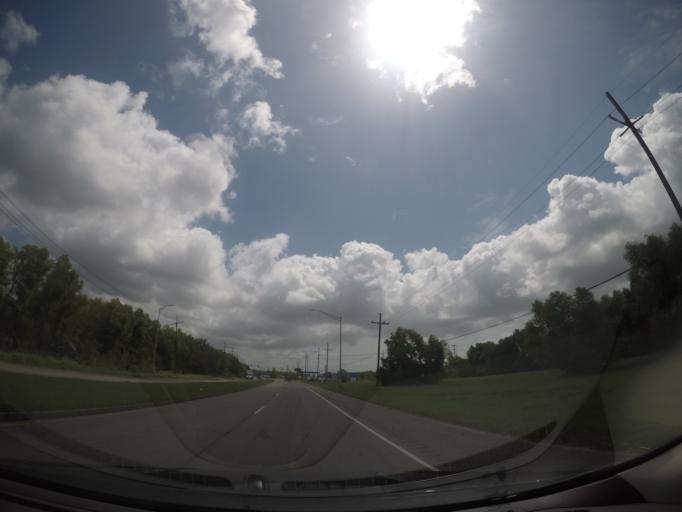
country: US
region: Louisiana
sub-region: Saint Bernard Parish
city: Chalmette
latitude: 30.0406
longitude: -89.8986
